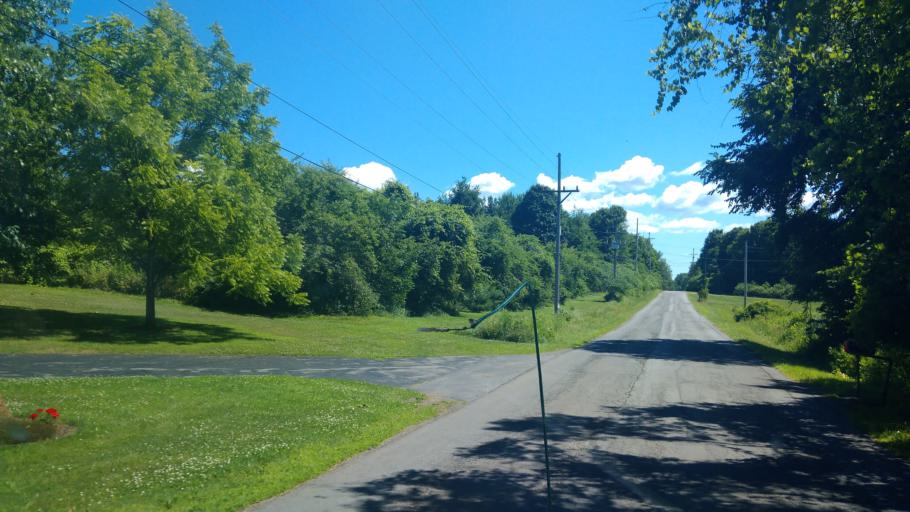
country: US
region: New York
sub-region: Wayne County
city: Sodus
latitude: 43.2410
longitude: -77.0228
